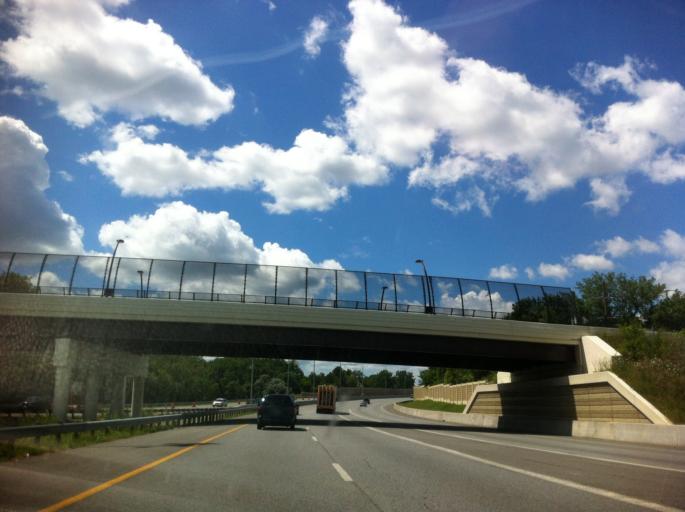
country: US
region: Ohio
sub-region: Lucas County
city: Toledo
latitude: 41.6758
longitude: -83.5785
